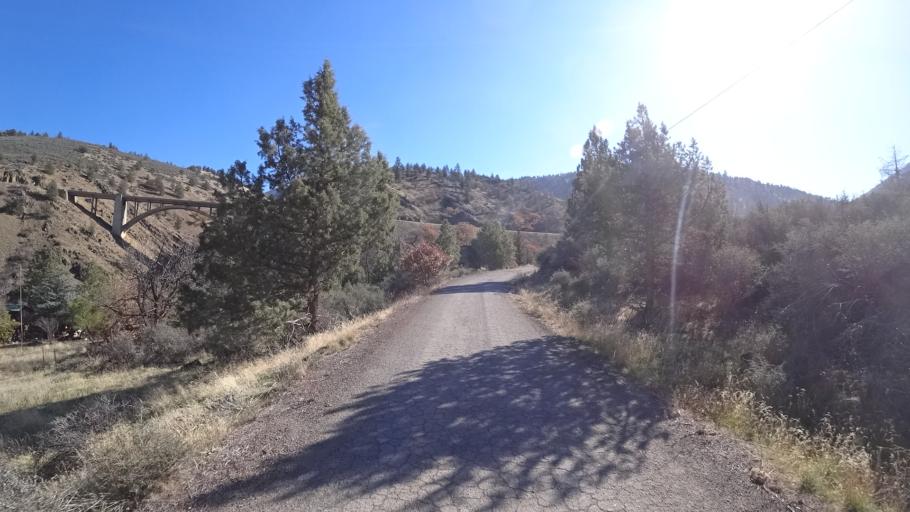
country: US
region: California
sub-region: Siskiyou County
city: Yreka
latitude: 41.8028
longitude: -122.6014
